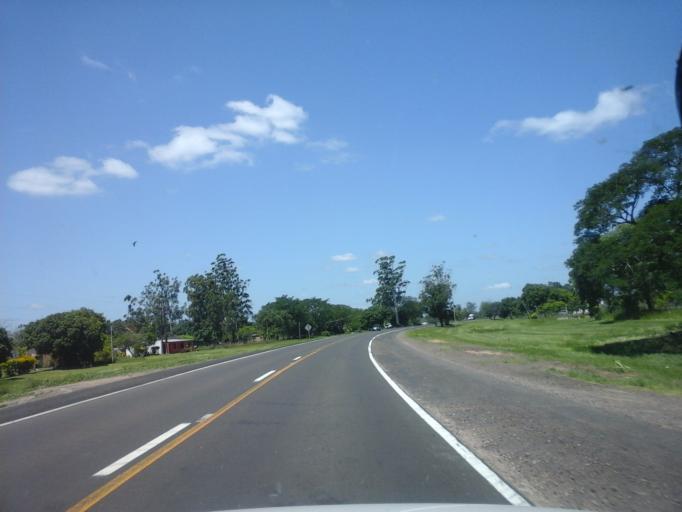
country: AR
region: Corrientes
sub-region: Departamento de Itati
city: Itati
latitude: -27.3580
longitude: -58.2618
